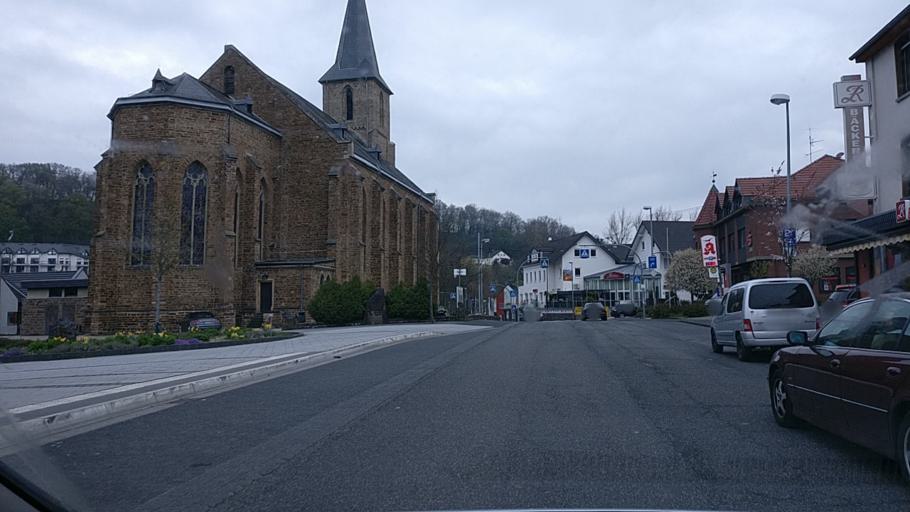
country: DE
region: Rheinland-Pfalz
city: Breitscheid
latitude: 50.6223
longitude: 7.4274
